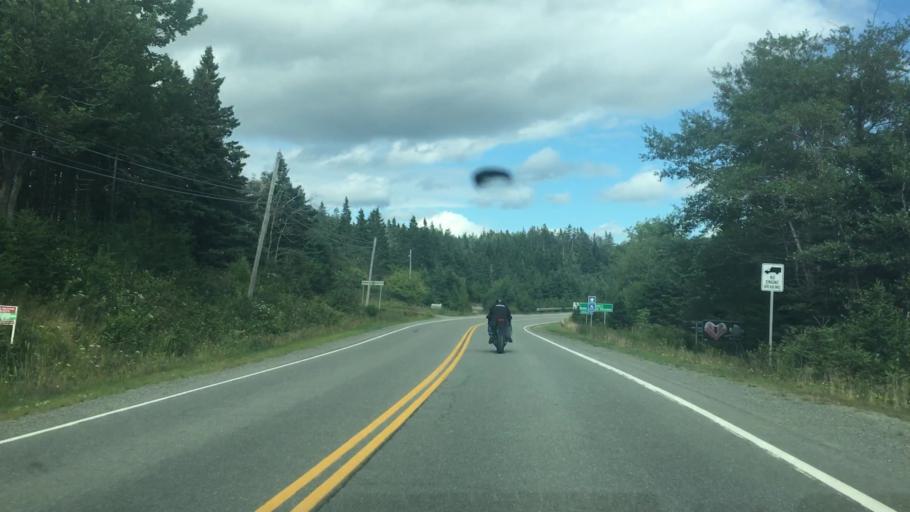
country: CA
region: Nova Scotia
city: Princeville
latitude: 45.6548
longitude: -60.8987
